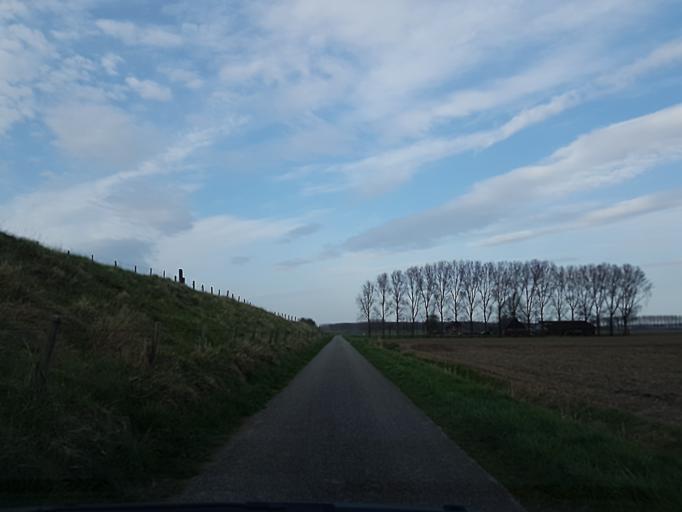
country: BE
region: Flanders
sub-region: Provincie Oost-Vlaanderen
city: Assenede
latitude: 51.2849
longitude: 3.7653
